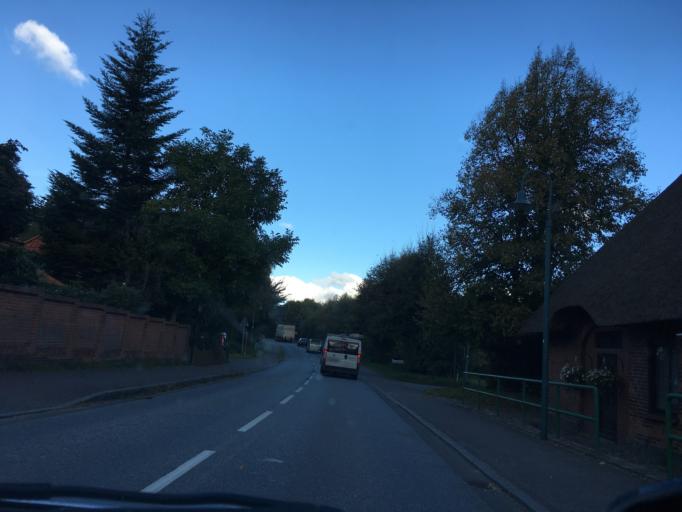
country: DE
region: Schleswig-Holstein
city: Achterwehr
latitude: 54.3146
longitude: 9.9632
